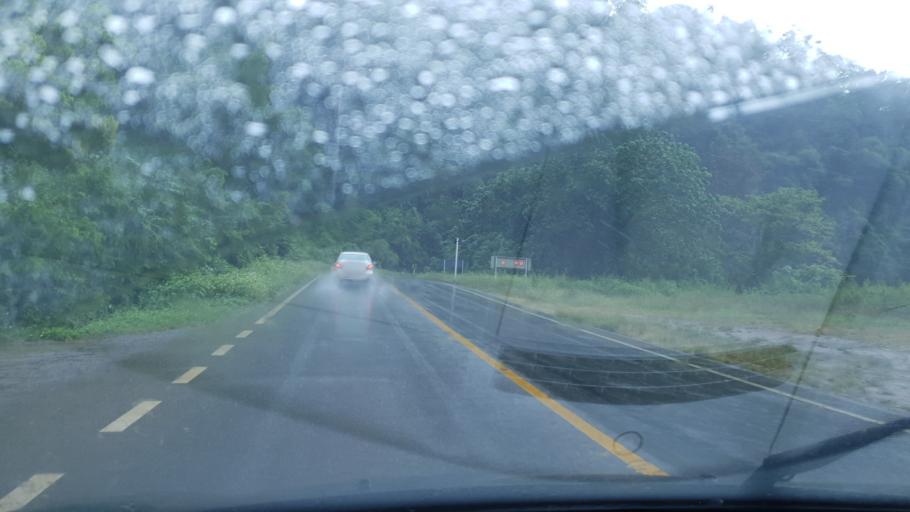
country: TH
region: Mae Hong Son
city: Khun Yuam
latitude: 18.6482
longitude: 97.9408
